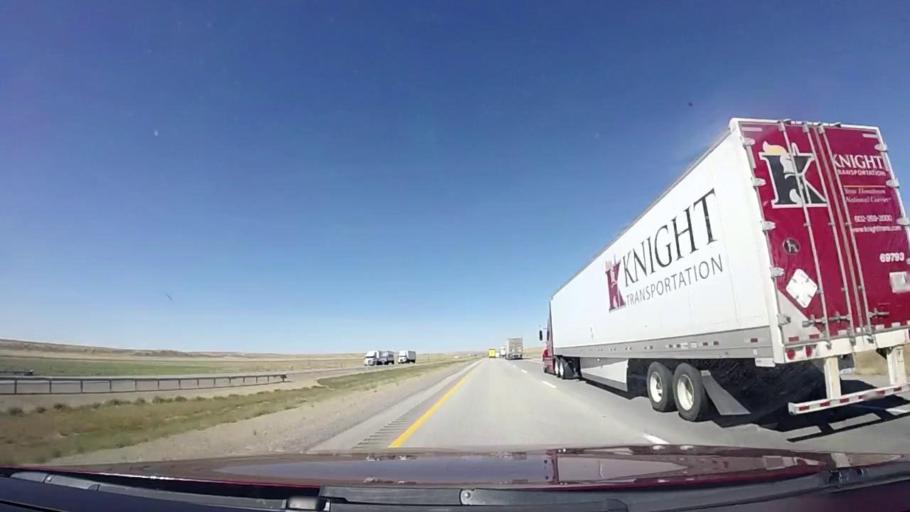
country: US
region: Wyoming
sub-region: Carbon County
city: Rawlins
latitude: 41.6655
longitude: -108.0331
